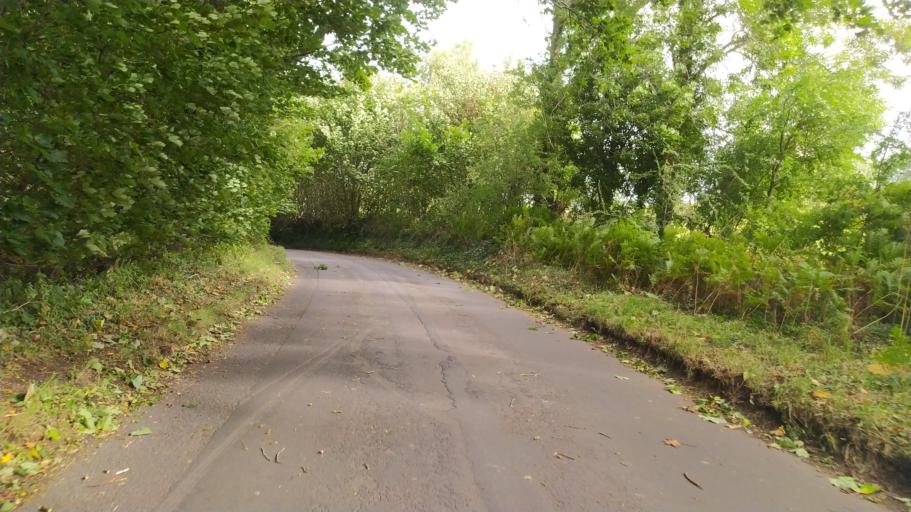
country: GB
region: England
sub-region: Dorset
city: Broadstone
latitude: 50.7681
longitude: -2.0291
